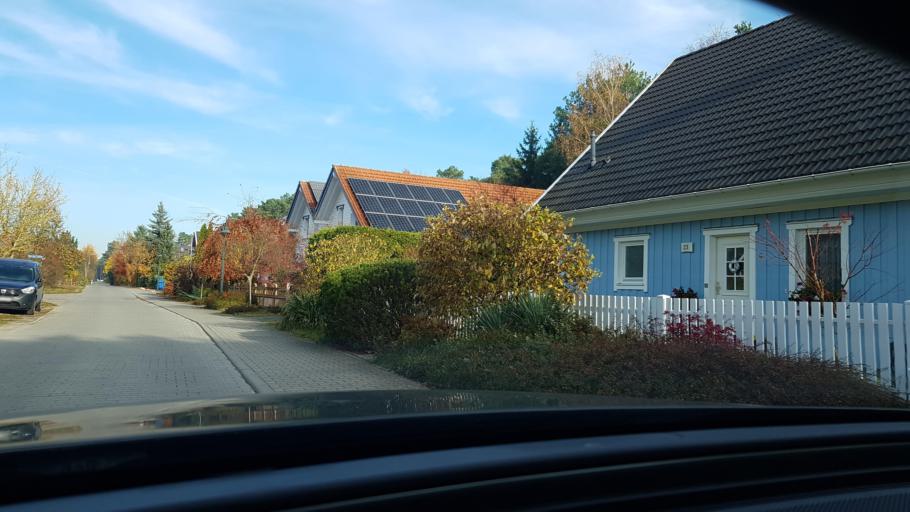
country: DE
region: Brandenburg
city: Borkwalde
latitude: 52.2537
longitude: 12.8428
